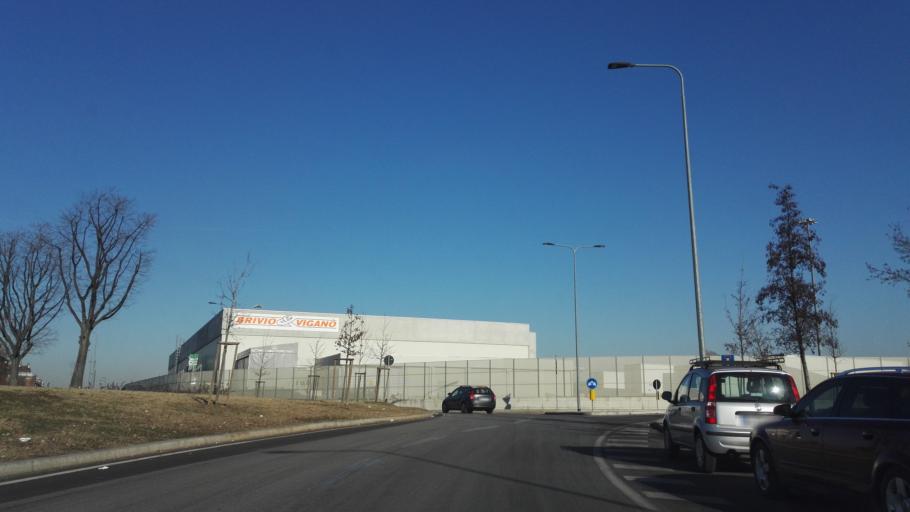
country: IT
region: Lombardy
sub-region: Citta metropolitana di Milano
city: Chiaravalle
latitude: 45.4481
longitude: 9.2296
